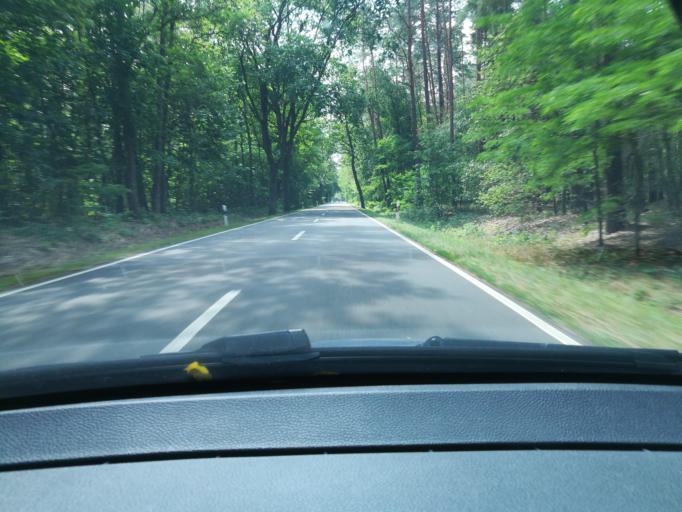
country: DE
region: Brandenburg
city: Wittstock
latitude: 53.0603
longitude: 12.4693
